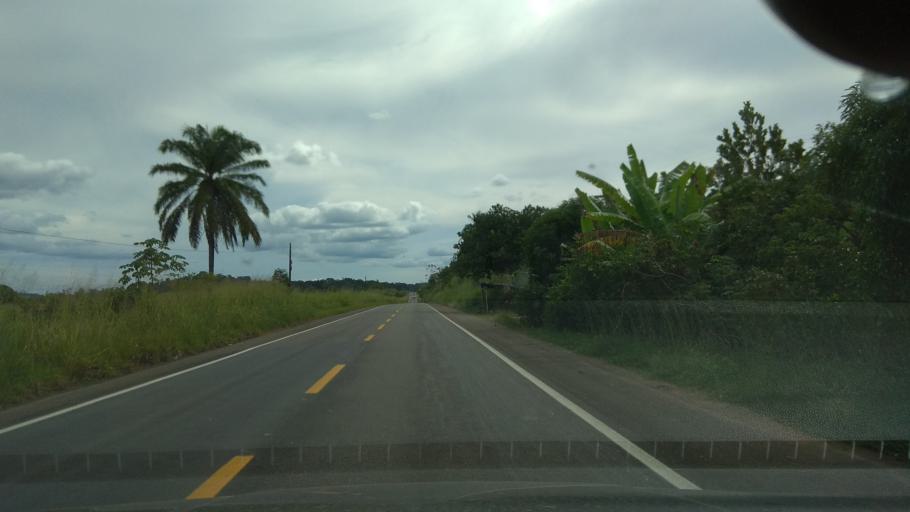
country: BR
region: Bahia
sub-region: Ubata
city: Ubata
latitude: -14.1960
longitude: -39.6294
